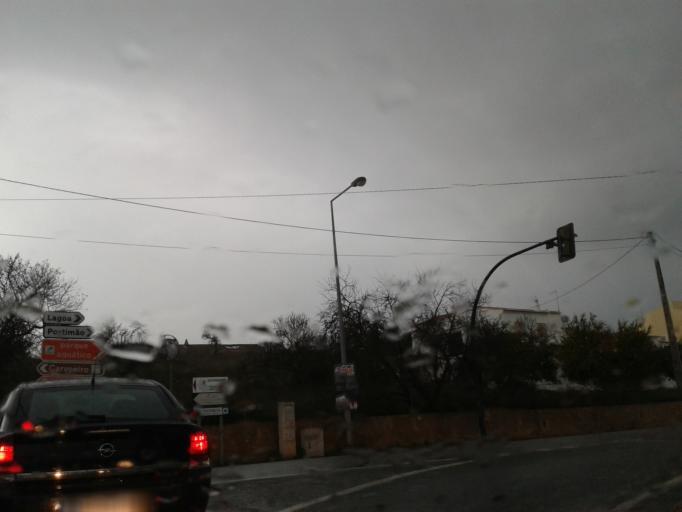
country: PT
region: Faro
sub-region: Lagoa
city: Carvoeiro
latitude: 37.1114
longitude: -8.4561
